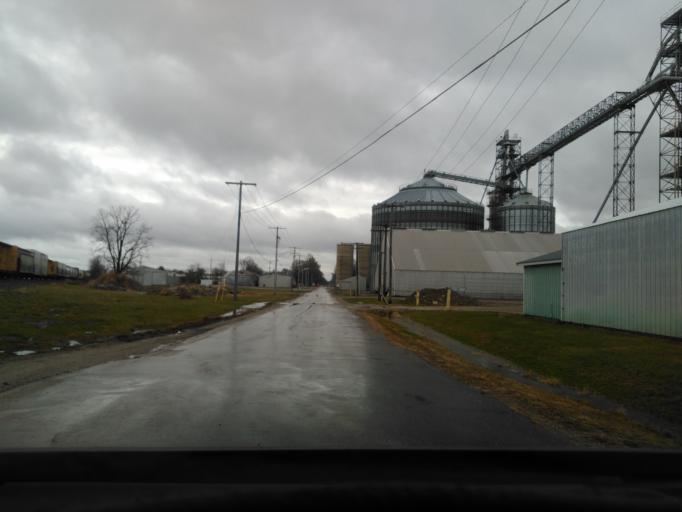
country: US
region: Illinois
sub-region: Effingham County
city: Altamont
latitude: 39.0595
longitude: -88.7555
